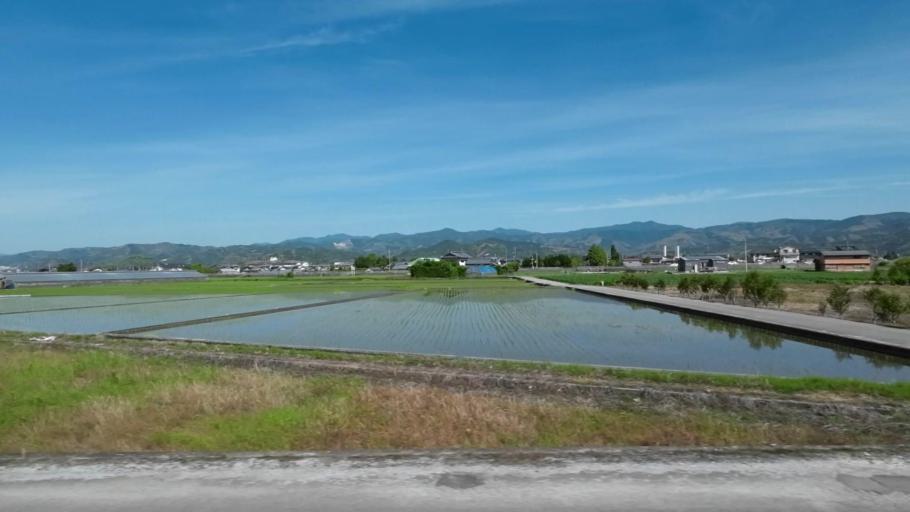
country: JP
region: Kochi
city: Kochi-shi
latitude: 33.5888
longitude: 133.6589
